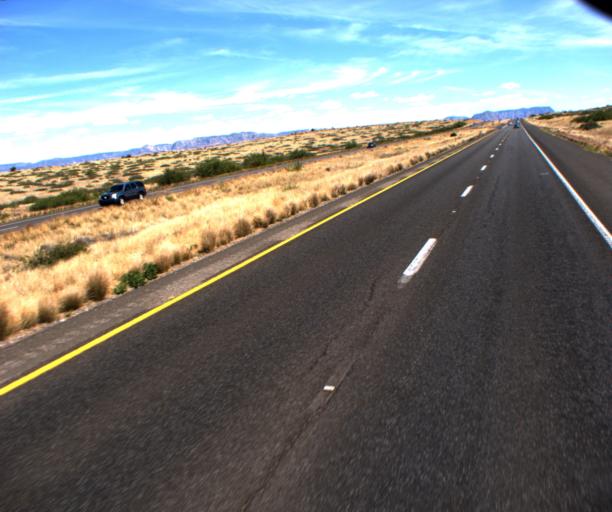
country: US
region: Arizona
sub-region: Yavapai County
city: Cornville
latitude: 34.7544
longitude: -111.9558
